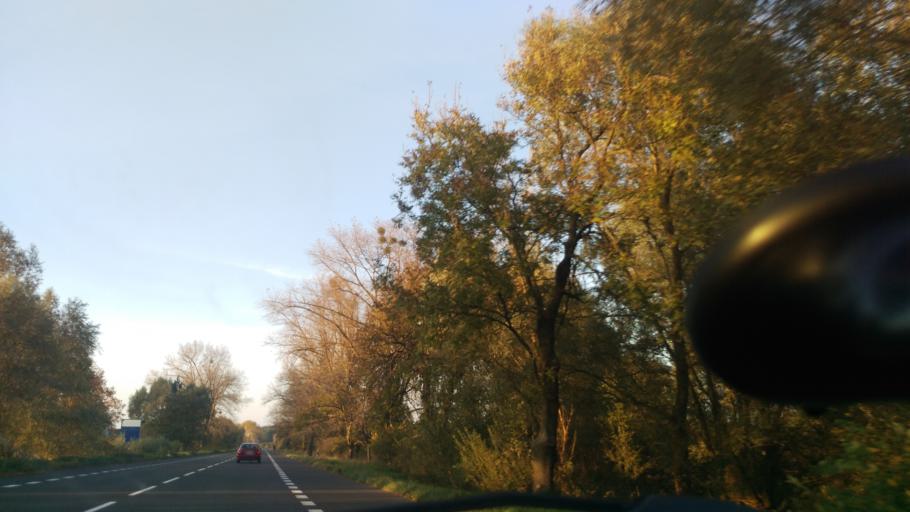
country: PL
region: West Pomeranian Voivodeship
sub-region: Powiat gryfinski
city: Stare Czarnowo
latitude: 53.2425
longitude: 14.7822
